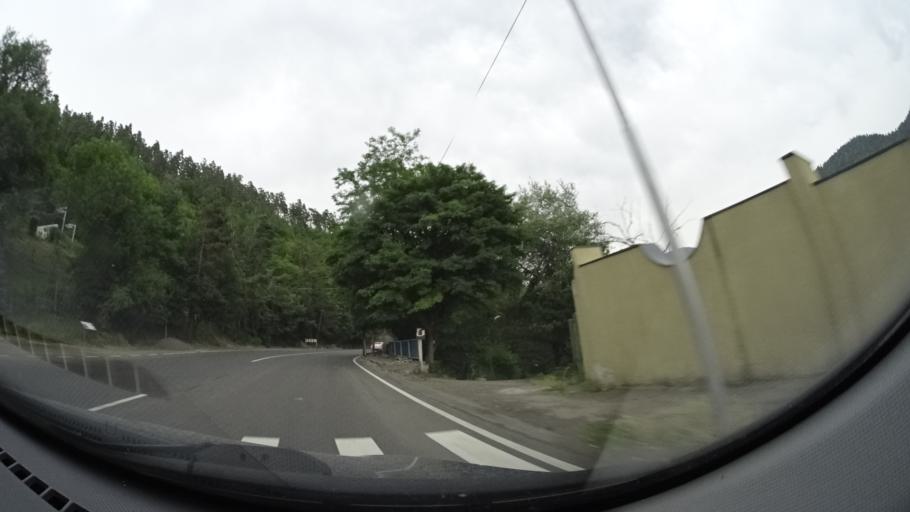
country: GE
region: Samtskhe-Javakheti
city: Borjomi
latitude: 41.8365
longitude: 43.3713
